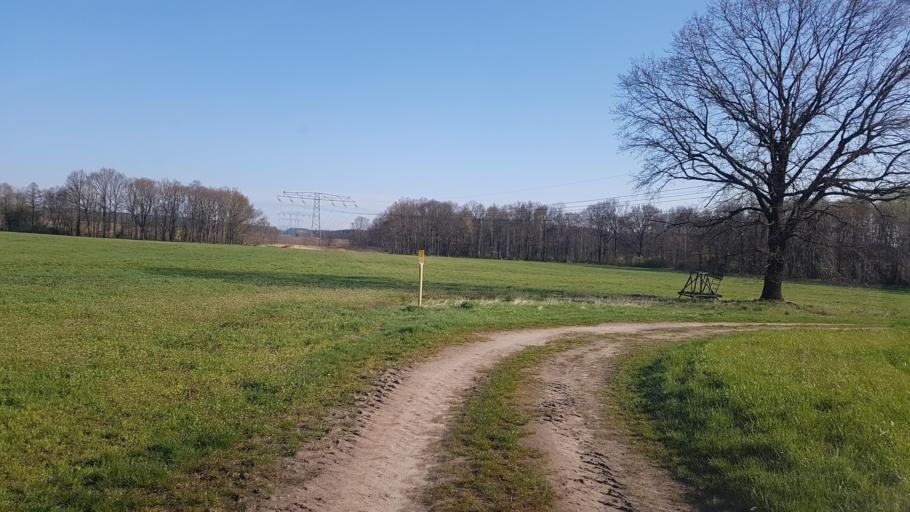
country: DE
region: Brandenburg
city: Altdobern
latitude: 51.6709
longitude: 13.9978
